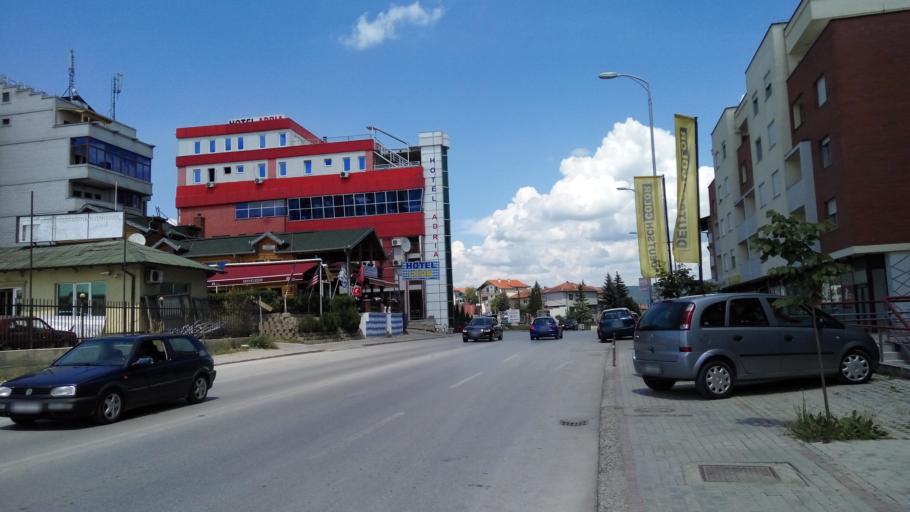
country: XK
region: Pristina
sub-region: Komuna e Prishtines
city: Pristina
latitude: 42.6600
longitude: 21.1486
